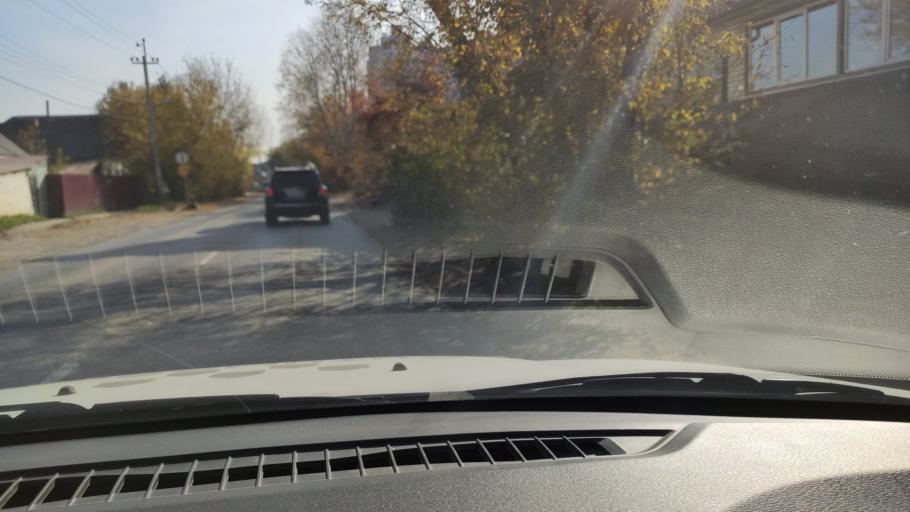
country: RU
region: Perm
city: Perm
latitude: 58.0081
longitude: 56.3242
